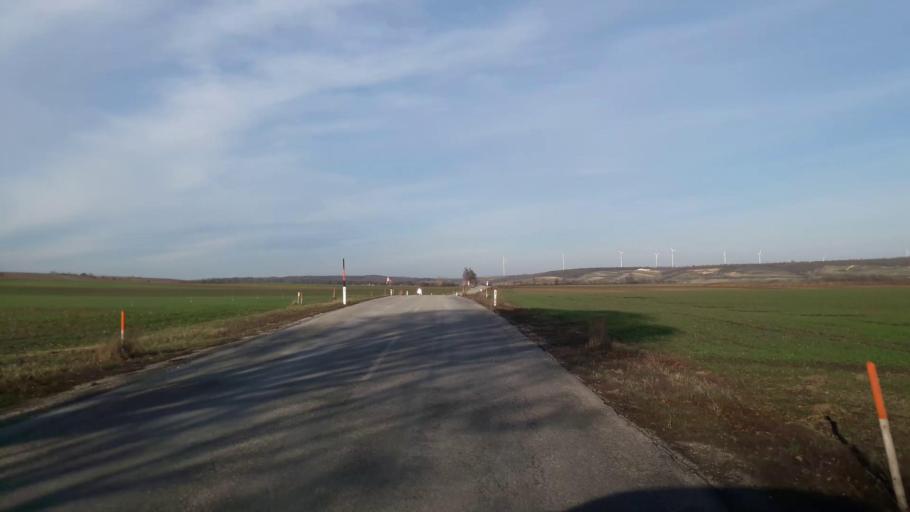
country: AT
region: Lower Austria
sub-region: Politischer Bezirk Ganserndorf
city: Gross-Schweinbarth
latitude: 48.3926
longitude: 16.6326
